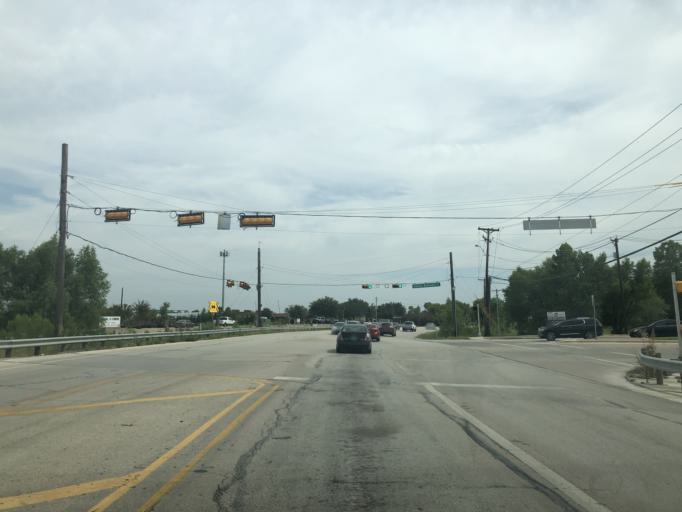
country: US
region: Texas
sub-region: Tarrant County
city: Blue Mound
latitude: 32.8842
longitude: -97.3429
